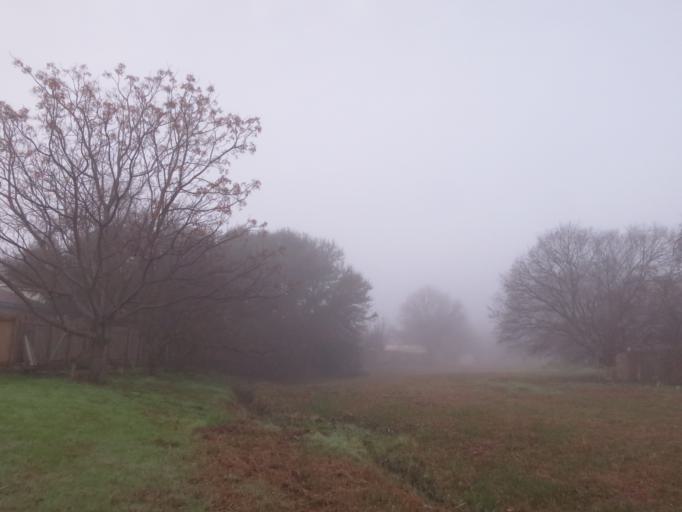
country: US
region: Texas
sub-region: Travis County
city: Wells Branch
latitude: 30.4209
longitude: -97.6851
